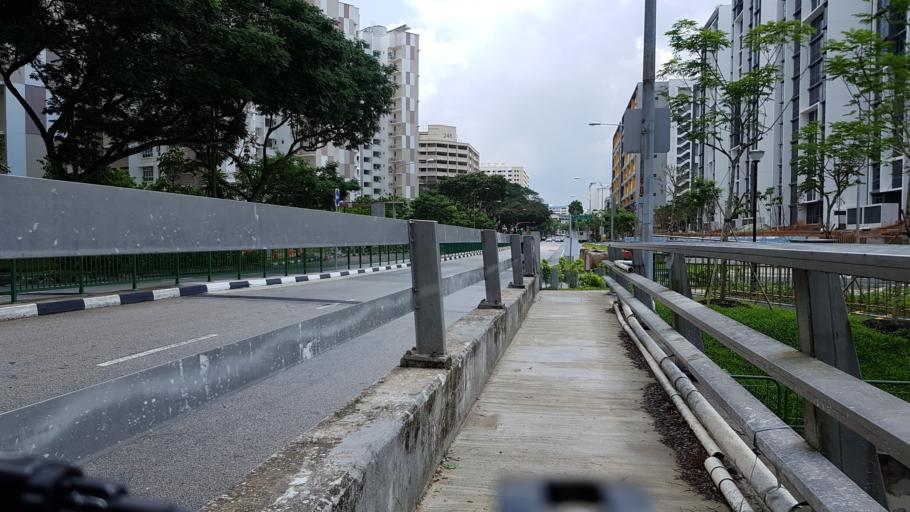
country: MY
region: Johor
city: Kampung Pasir Gudang Baru
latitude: 1.4338
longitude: 103.8446
